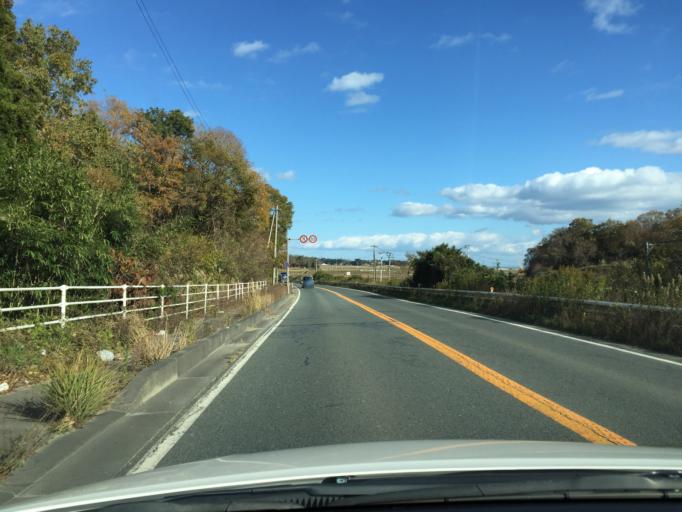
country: JP
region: Fukushima
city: Namie
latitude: 37.5751
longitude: 141.0083
